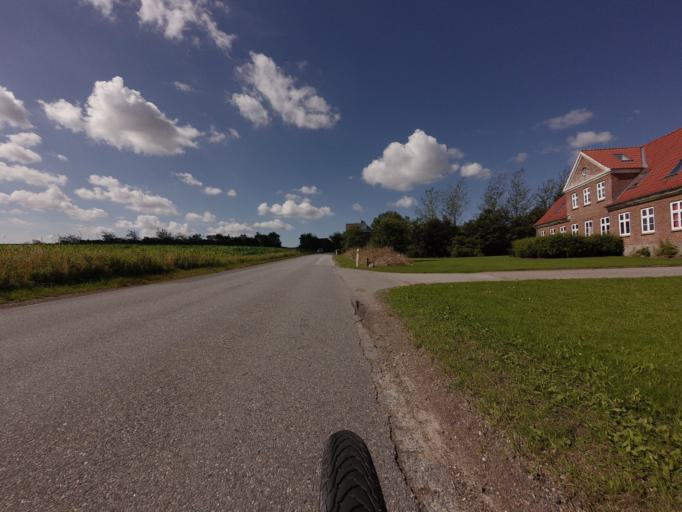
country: DK
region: North Denmark
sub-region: Hjorring Kommune
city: Hjorring
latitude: 57.4794
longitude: 9.9130
